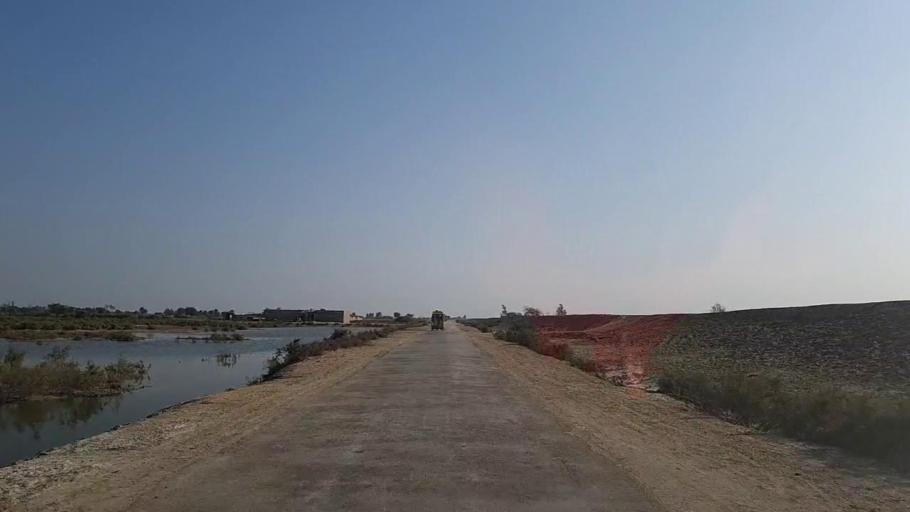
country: PK
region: Sindh
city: Sanghar
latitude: 25.9576
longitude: 69.0413
